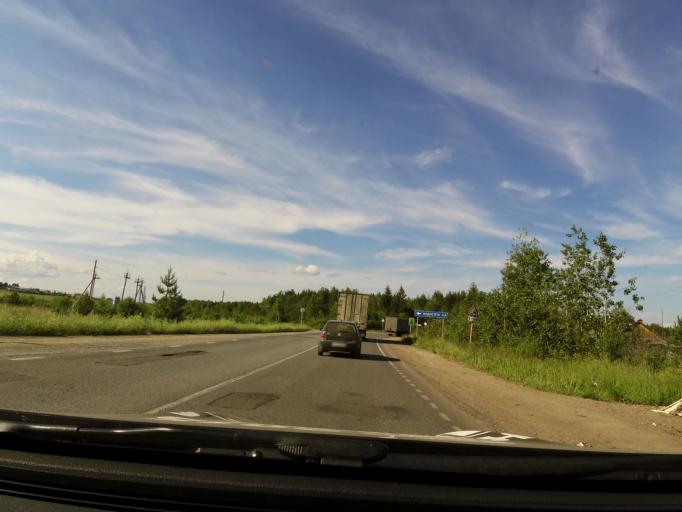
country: RU
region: Kirov
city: Belaya Kholunitsa
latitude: 58.8687
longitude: 50.8435
